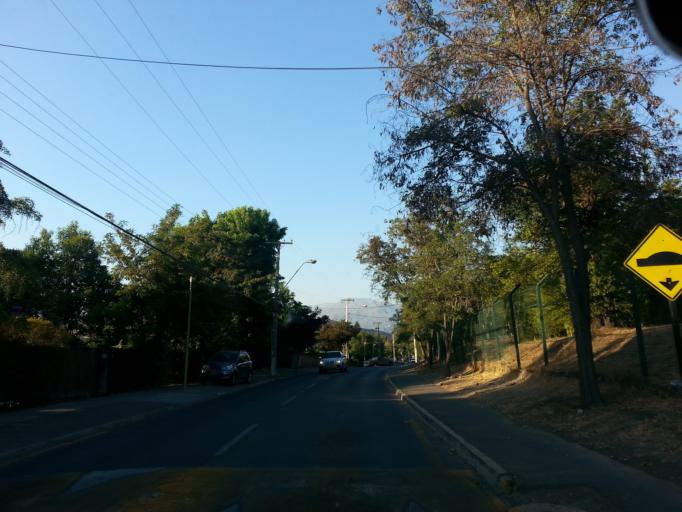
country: CL
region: Santiago Metropolitan
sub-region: Provincia de Santiago
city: Villa Presidente Frei, Nunoa, Santiago, Chile
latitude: -33.3944
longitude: -70.5396
